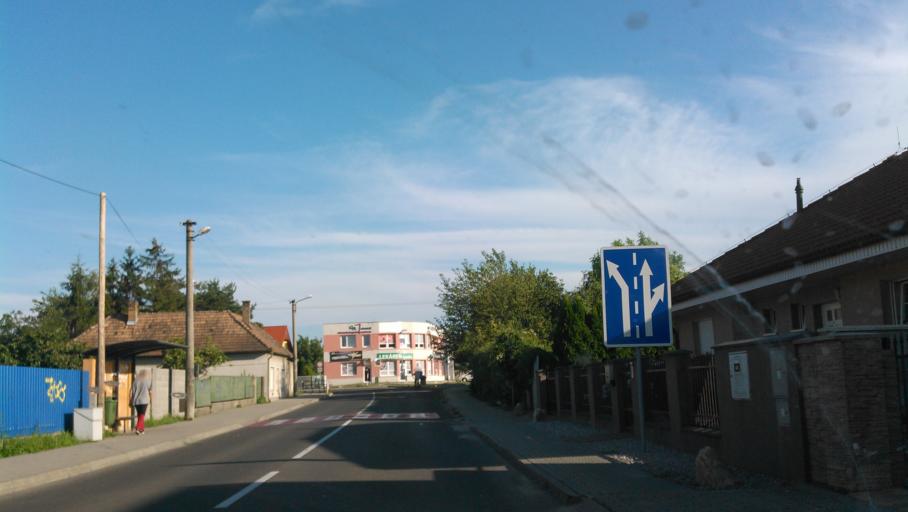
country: SK
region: Bratislavsky
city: Svaty Jur
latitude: 48.1899
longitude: 17.2502
